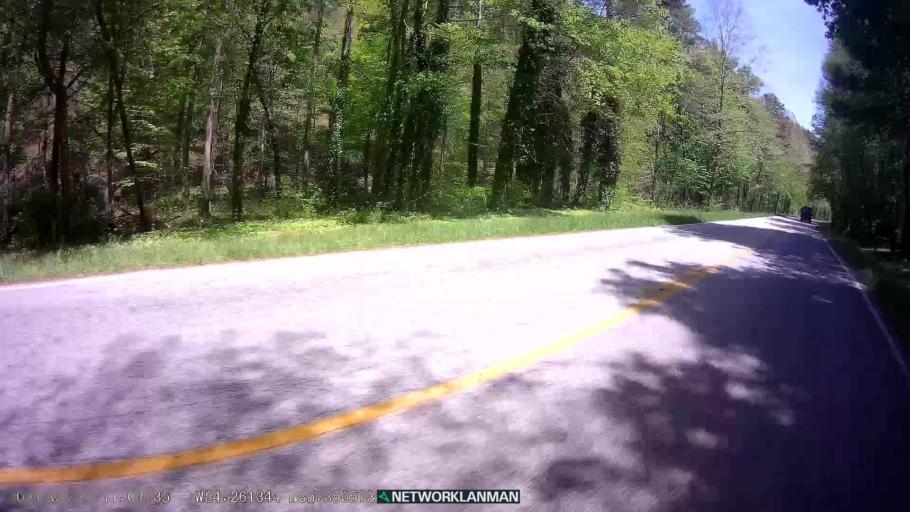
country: US
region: Tennessee
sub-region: Monroe County
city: Madisonville
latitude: 35.3535
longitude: -84.2611
